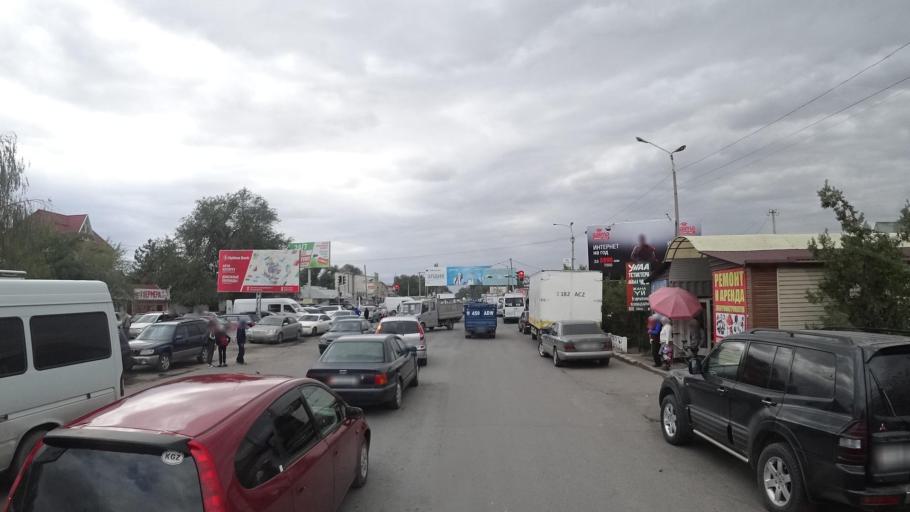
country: KG
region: Chuy
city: Kara-Balta
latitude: 42.8248
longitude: 73.8445
